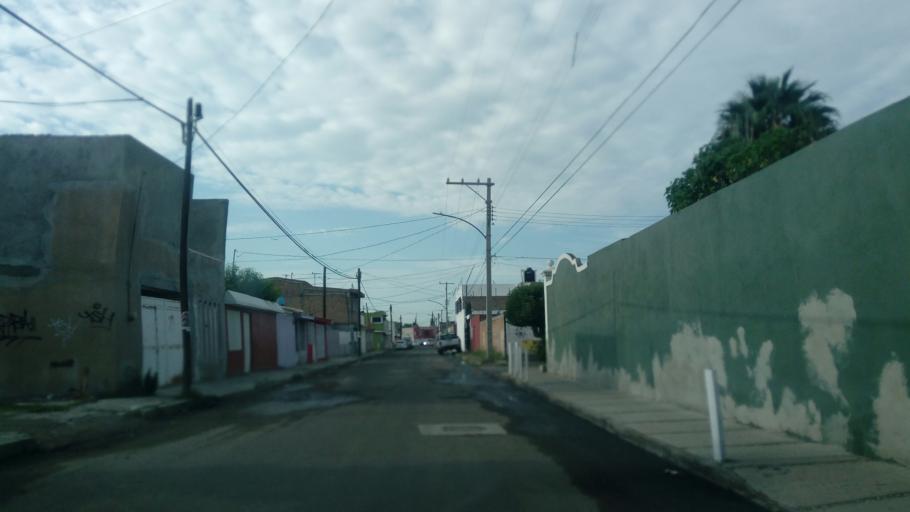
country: MX
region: Durango
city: Victoria de Durango
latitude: 24.0185
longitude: -104.6481
